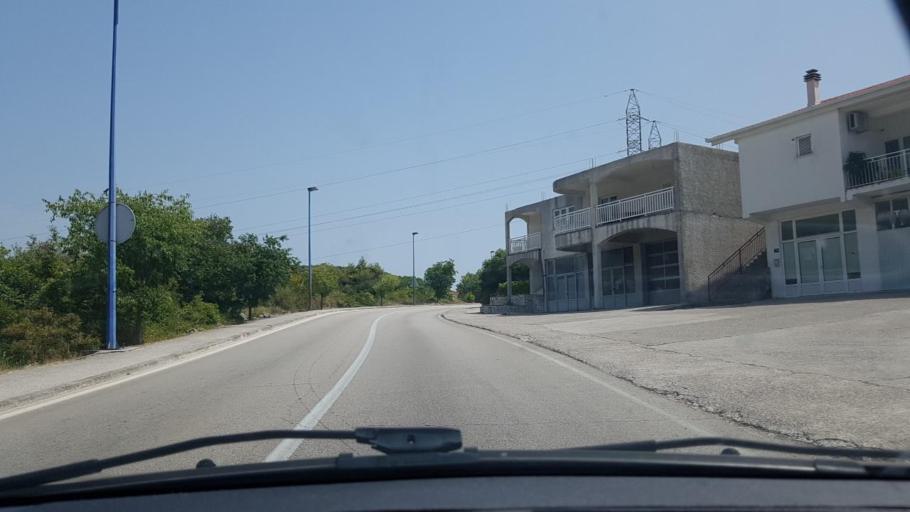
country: BA
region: Federation of Bosnia and Herzegovina
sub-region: Hercegovacko-Bosanski Kanton
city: Neum
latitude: 42.9263
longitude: 17.6197
